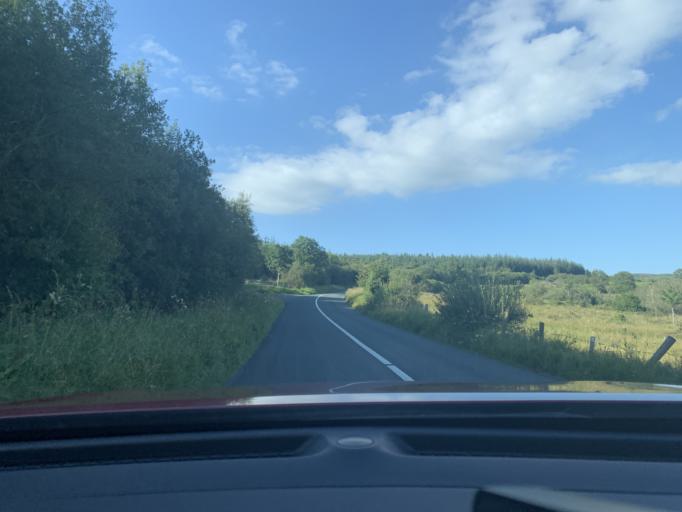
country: IE
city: Ballisodare
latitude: 54.1842
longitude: -8.5890
